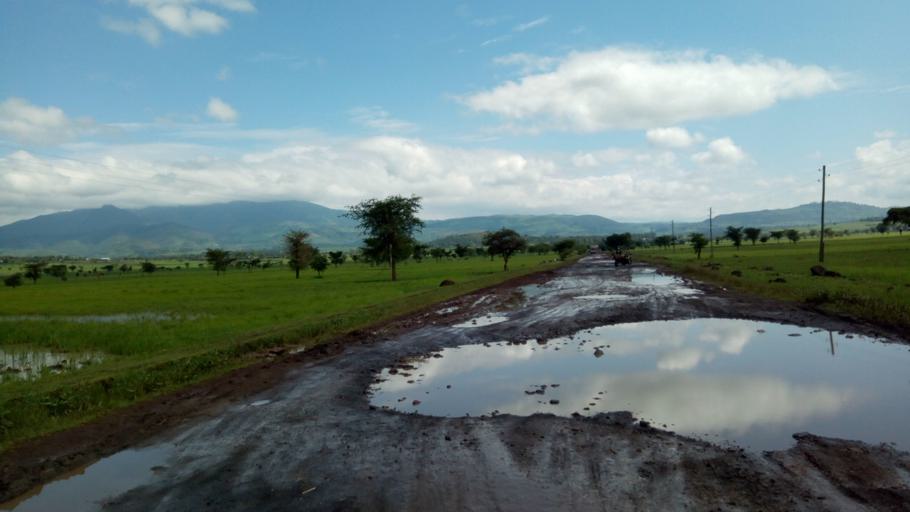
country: ET
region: Oromiya
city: Bishoftu
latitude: 8.8069
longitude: 39.0038
